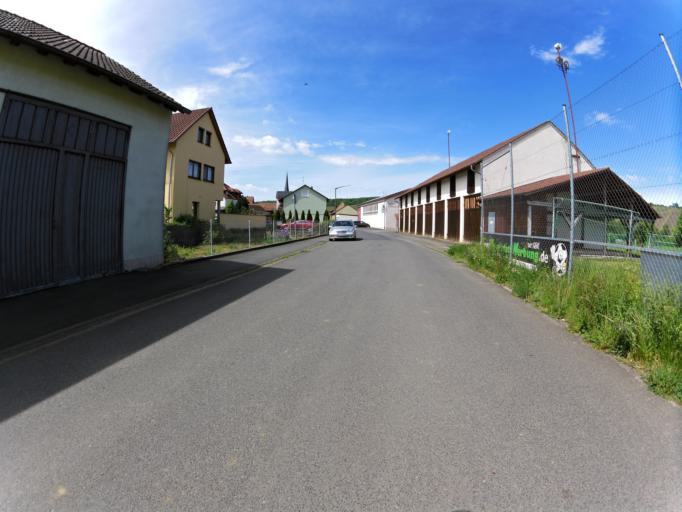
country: DE
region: Bavaria
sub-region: Regierungsbezirk Unterfranken
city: Nordheim
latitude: 49.8611
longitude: 10.1866
